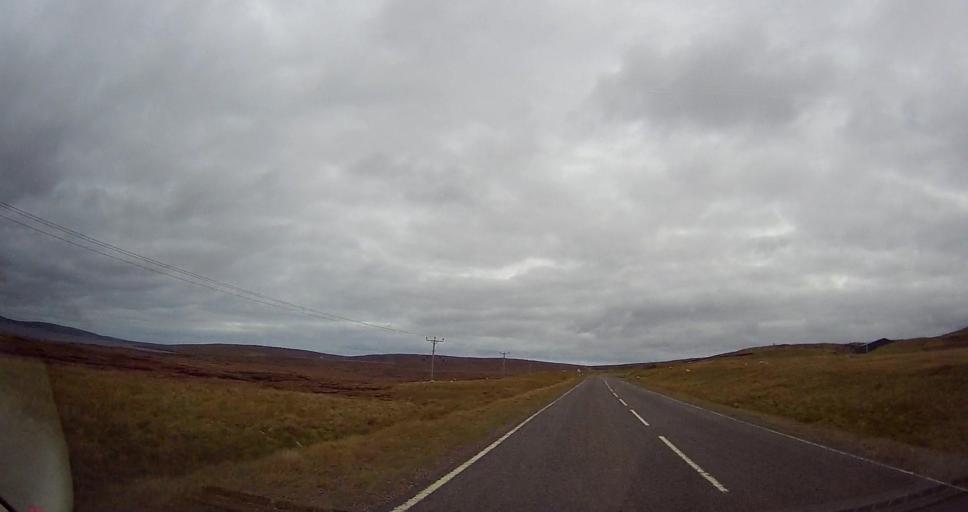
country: GB
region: Scotland
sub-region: Shetland Islands
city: Shetland
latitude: 60.6516
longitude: -1.0667
